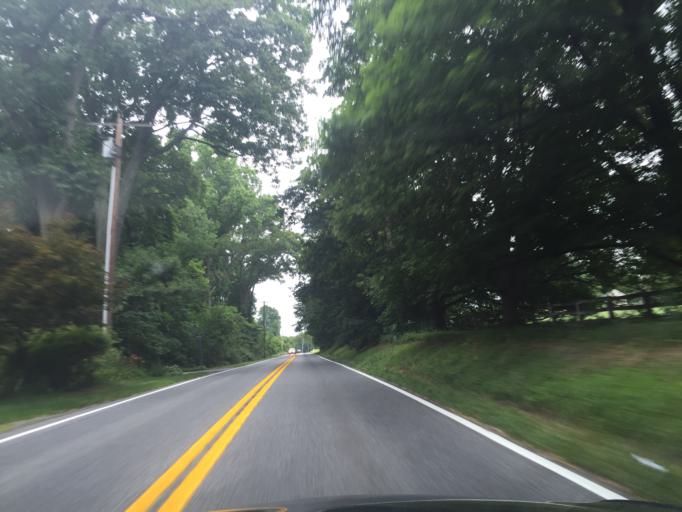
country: US
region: Maryland
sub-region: Harford County
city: Jarrettsville
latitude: 39.5646
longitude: -76.5232
